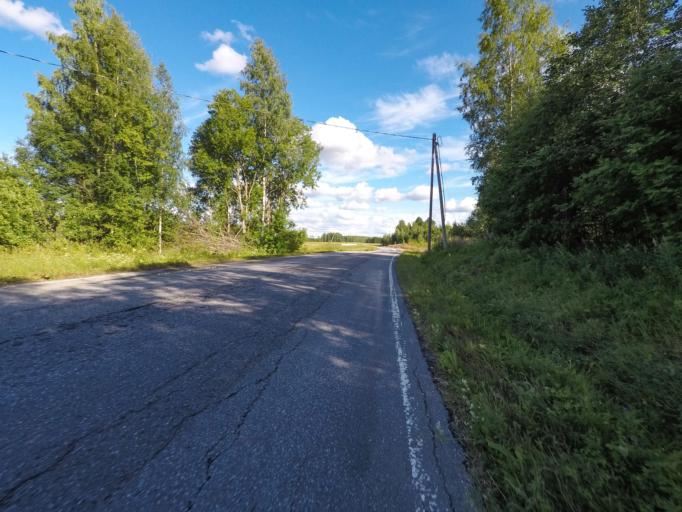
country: FI
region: South Karelia
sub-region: Imatra
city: Imatra
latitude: 61.1392
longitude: 28.6471
